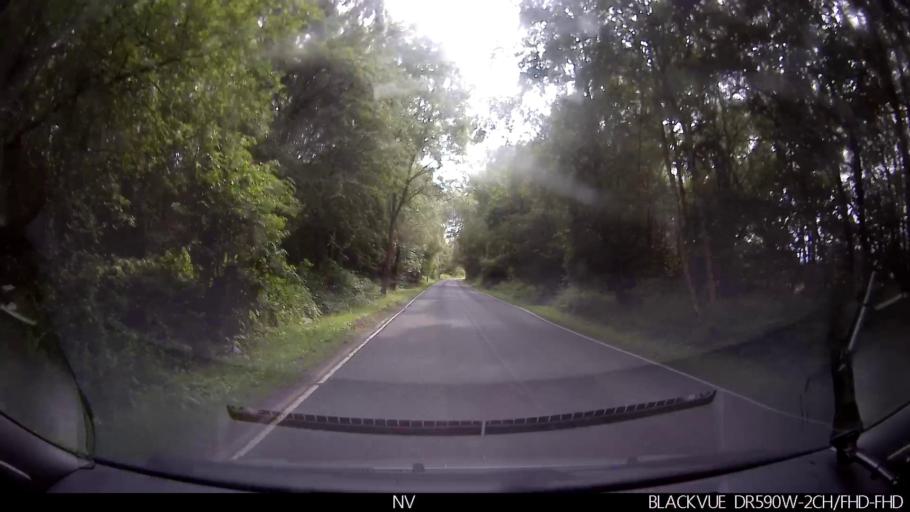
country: GB
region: England
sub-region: North Yorkshire
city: Strensall
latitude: 54.0335
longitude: -1.0286
